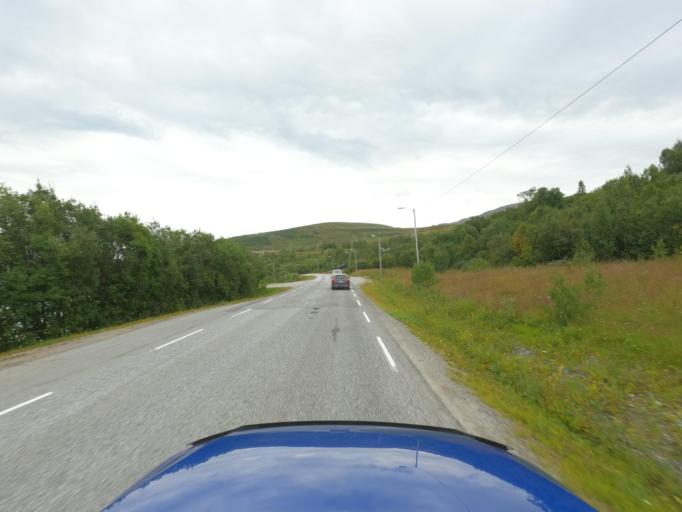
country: NO
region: Finnmark Fylke
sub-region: Kvalsund
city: Kvalsund
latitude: 70.4934
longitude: 24.0965
